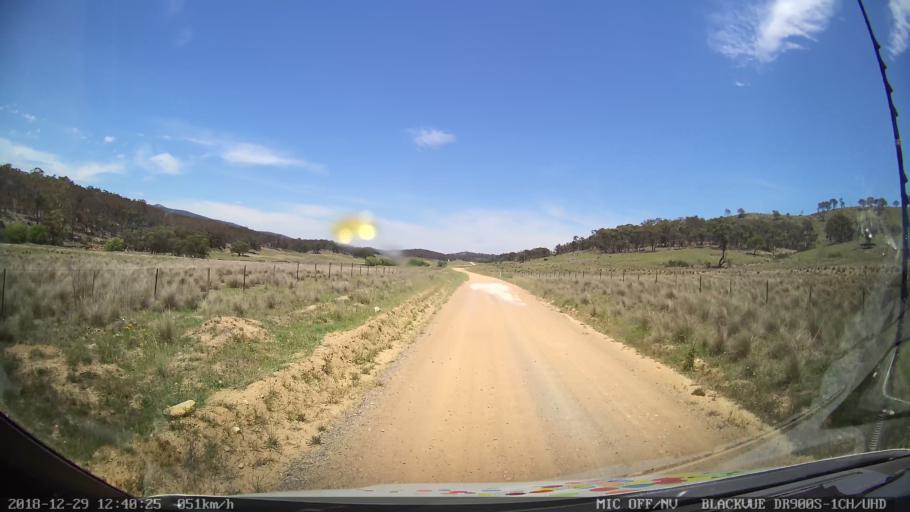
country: AU
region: Australian Capital Territory
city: Macarthur
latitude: -35.6011
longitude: 149.2249
